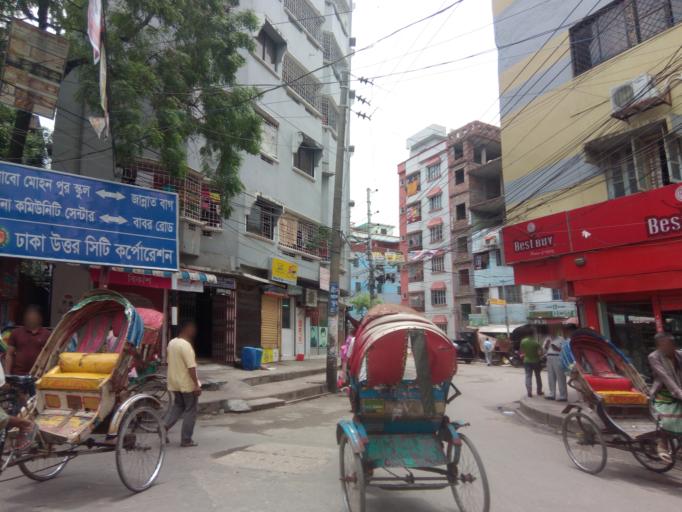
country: BD
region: Dhaka
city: Azimpur
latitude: 23.7682
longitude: 90.3625
